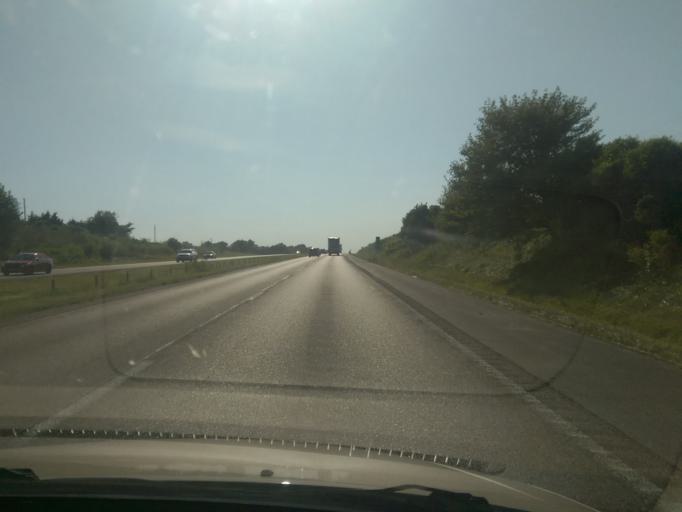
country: US
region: Missouri
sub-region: Lafayette County
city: Higginsville
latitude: 39.0022
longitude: -93.7935
